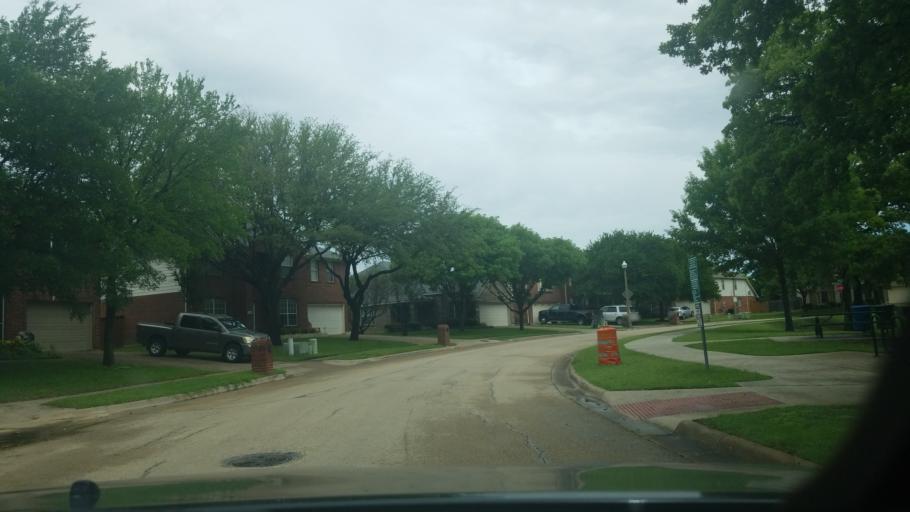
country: US
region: Texas
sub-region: Denton County
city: Copper Canyon
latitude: 33.1492
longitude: -97.1252
